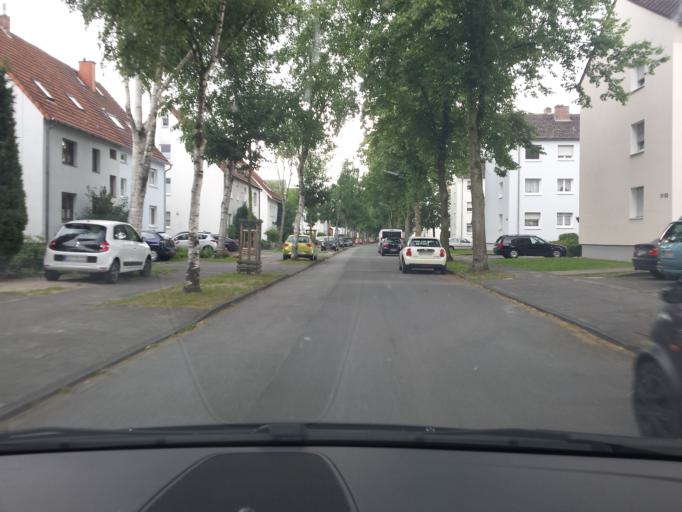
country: DE
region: North Rhine-Westphalia
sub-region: Regierungsbezirk Arnsberg
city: Lippstadt
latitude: 51.6767
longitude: 8.3252
